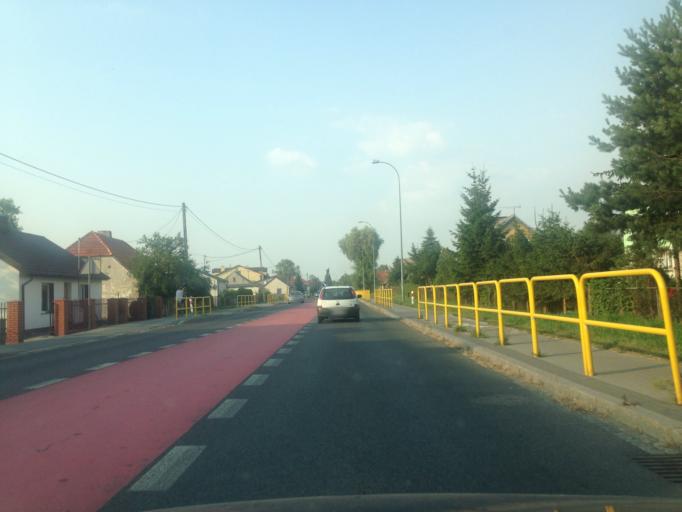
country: PL
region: Kujawsko-Pomorskie
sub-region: Powiat wloclawski
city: Fabianki
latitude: 52.7162
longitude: 19.1072
